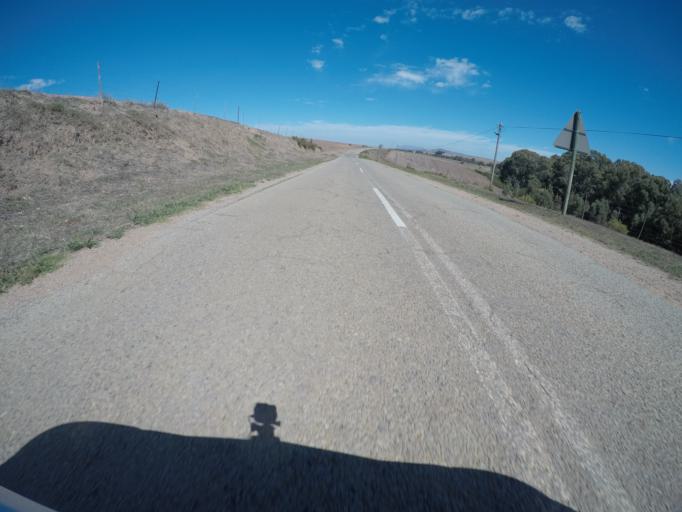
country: ZA
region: Western Cape
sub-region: City of Cape Town
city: Atlantis
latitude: -33.6140
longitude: 18.6359
